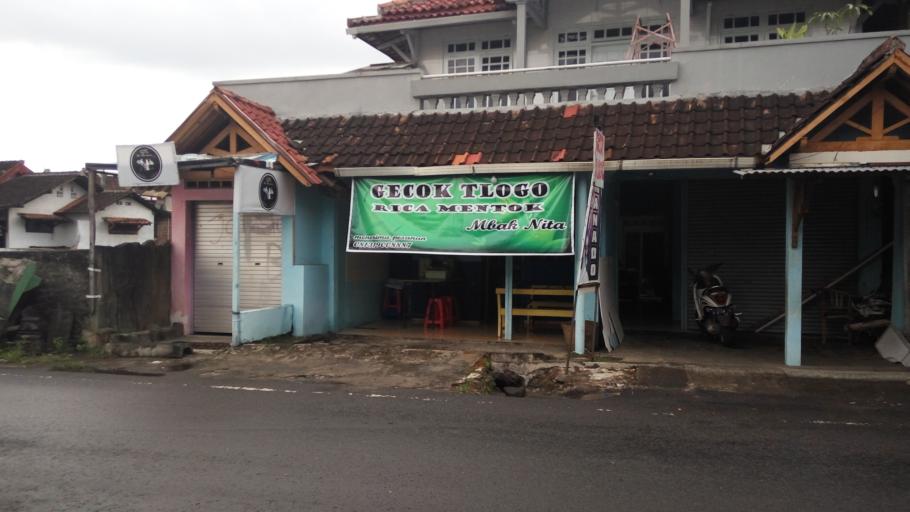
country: ID
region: Central Java
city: Ambarawa
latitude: -7.2626
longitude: 110.4061
